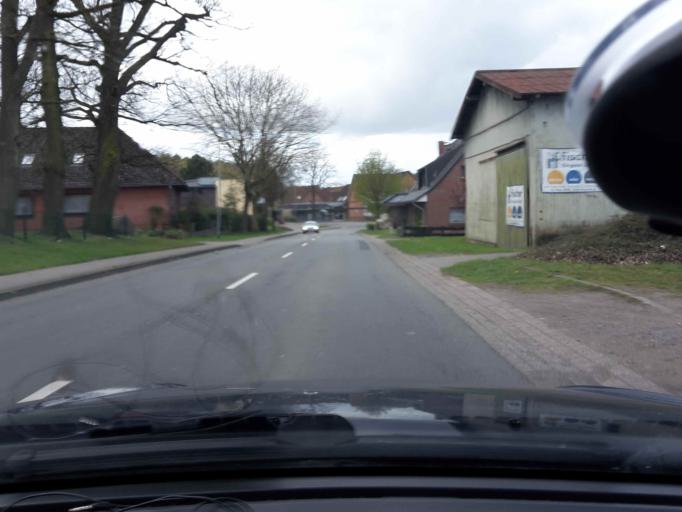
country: DE
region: Lower Saxony
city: Nottensdorf
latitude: 53.4797
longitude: 9.6194
